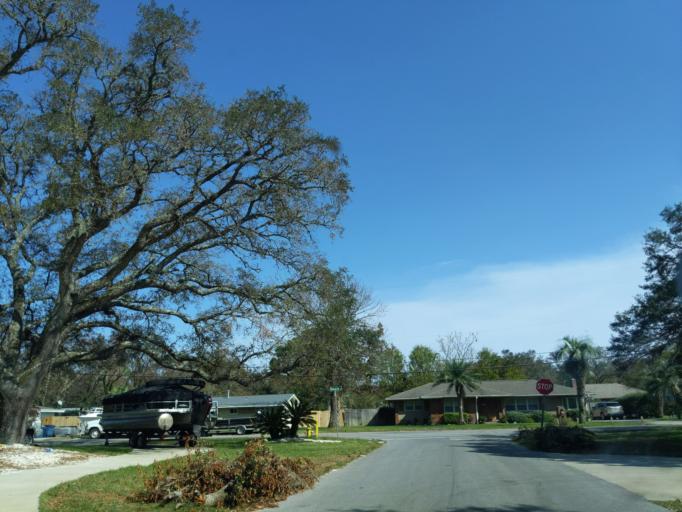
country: US
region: Florida
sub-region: Santa Rosa County
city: Gulf Breeze
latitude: 30.3541
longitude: -87.1880
